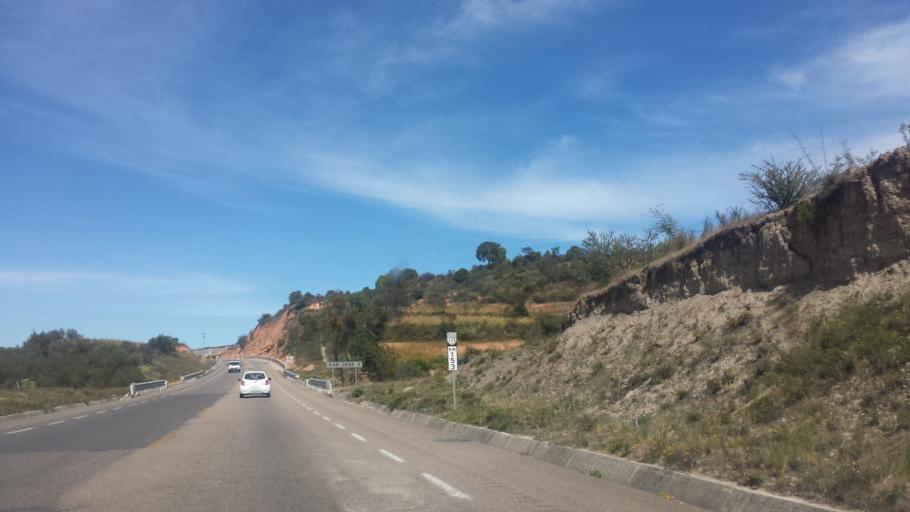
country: MX
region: Oaxaca
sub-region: Villa Tejupam de la Union
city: Villa Tejupam de la Union
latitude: 17.6347
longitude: -97.3350
